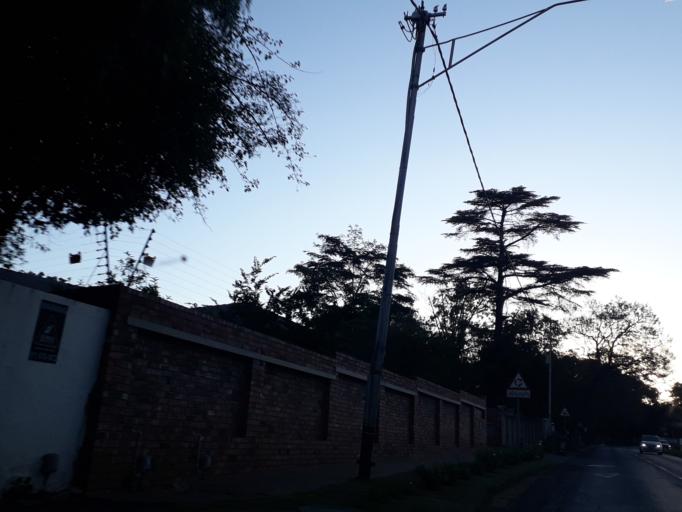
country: ZA
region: Gauteng
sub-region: City of Johannesburg Metropolitan Municipality
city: Roodepoort
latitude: -26.1357
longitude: 27.9675
